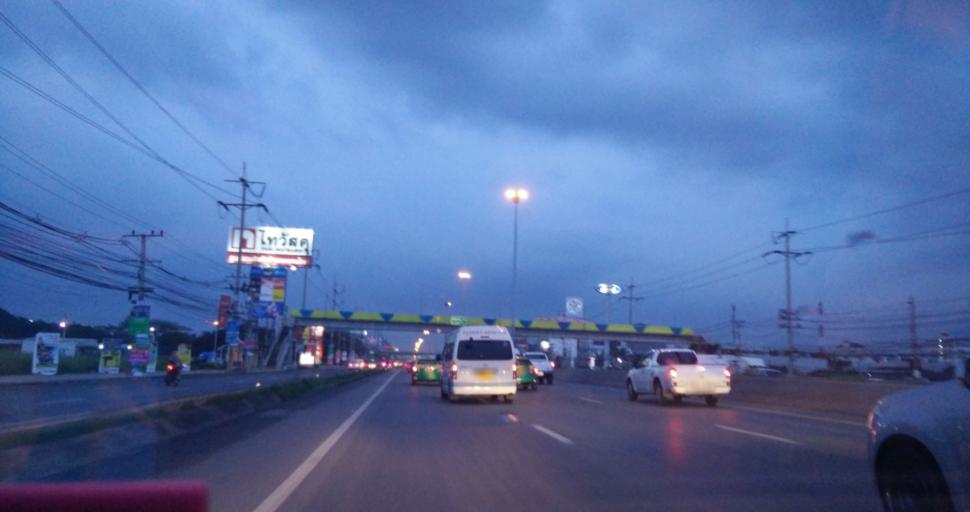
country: TH
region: Pathum Thani
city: Khlong Luang
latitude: 14.0150
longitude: 100.6153
